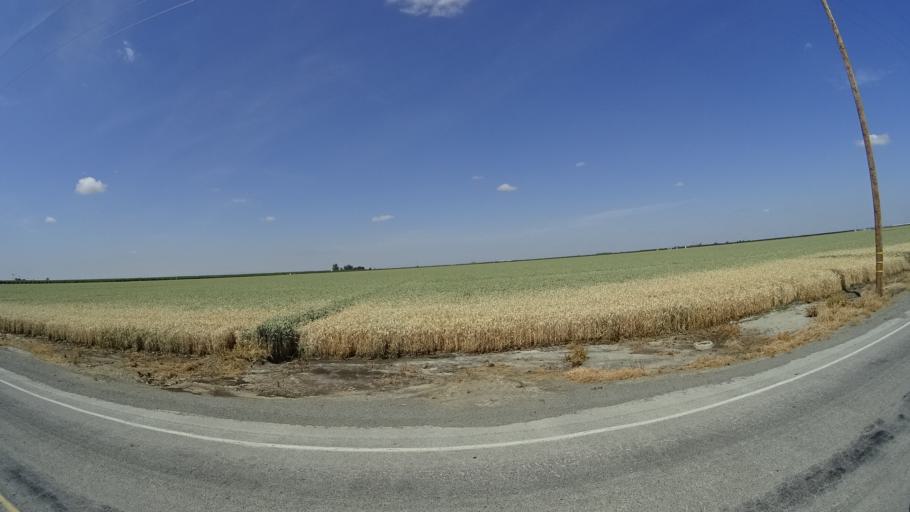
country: US
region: California
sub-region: Tulare County
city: Goshen
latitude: 36.2788
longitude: -119.4923
